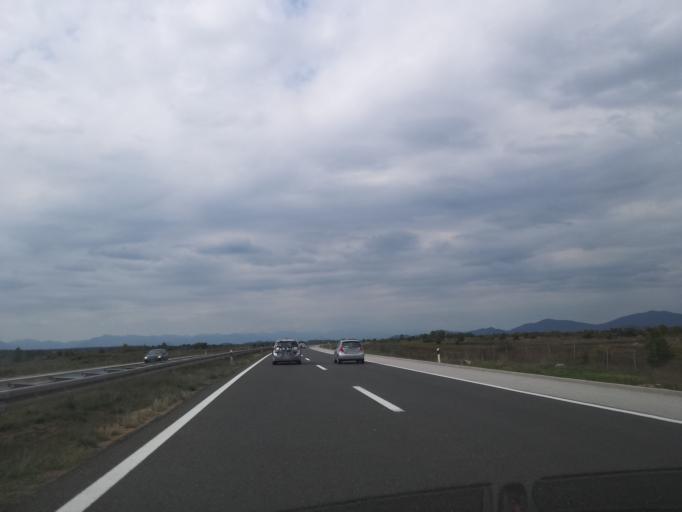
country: HR
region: Licko-Senjska
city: Gospic
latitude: 44.4817
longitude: 15.5578
